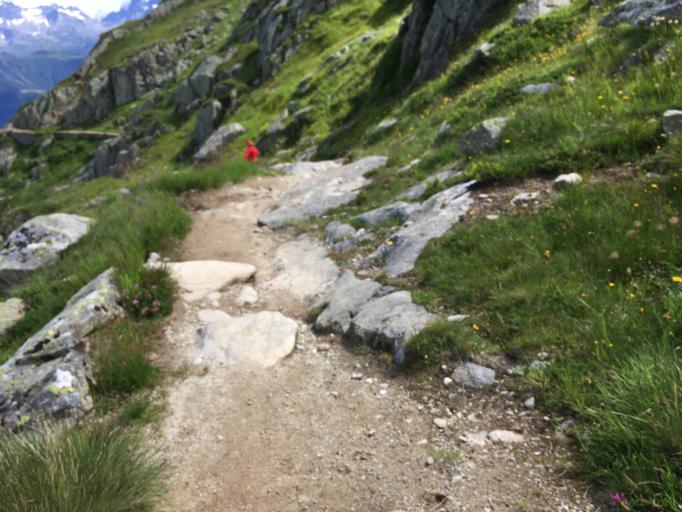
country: CH
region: Valais
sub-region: Goms District
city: Fiesch
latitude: 46.4445
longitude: 8.1193
